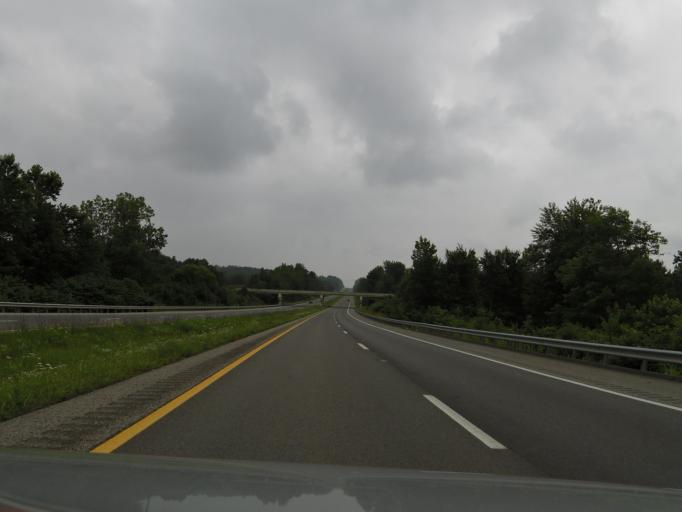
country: US
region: Kentucky
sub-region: Muhlenberg County
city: Morehead
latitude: 37.2473
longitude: -87.2392
